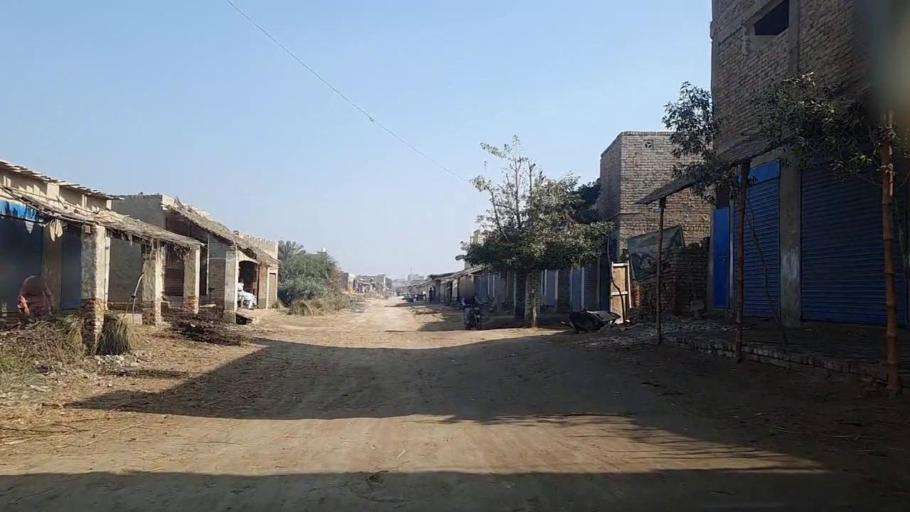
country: PK
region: Sindh
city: Khairpur
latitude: 27.9443
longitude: 69.6646
